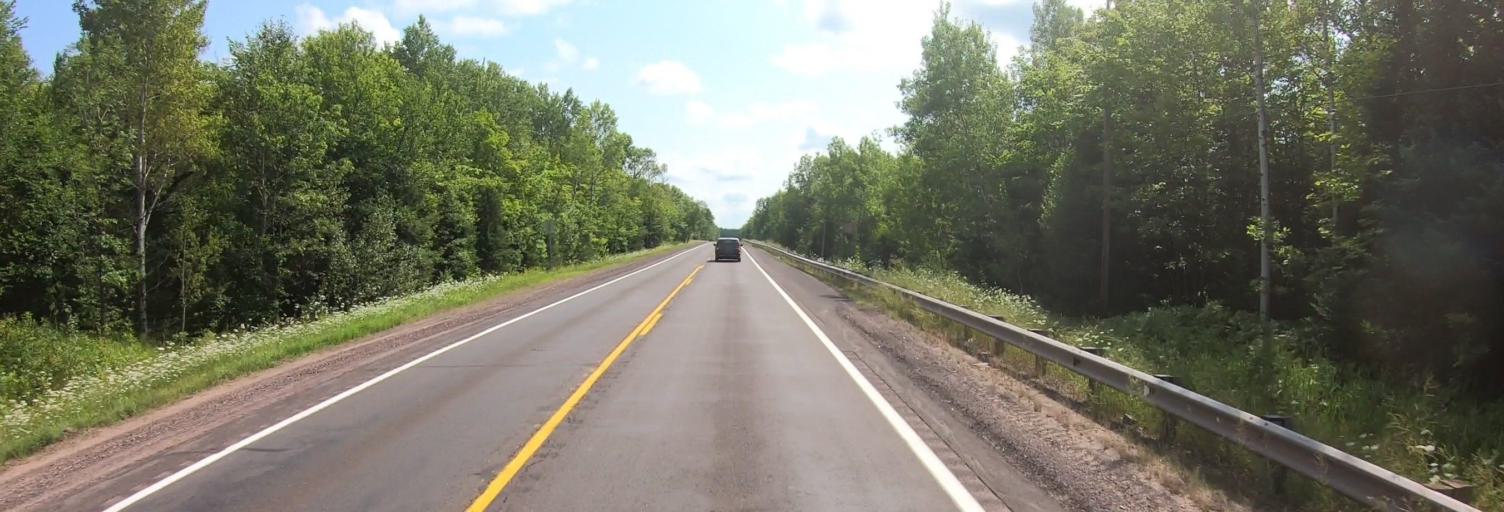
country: US
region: Michigan
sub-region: Ontonagon County
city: Ontonagon
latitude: 46.7513
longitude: -89.1009
